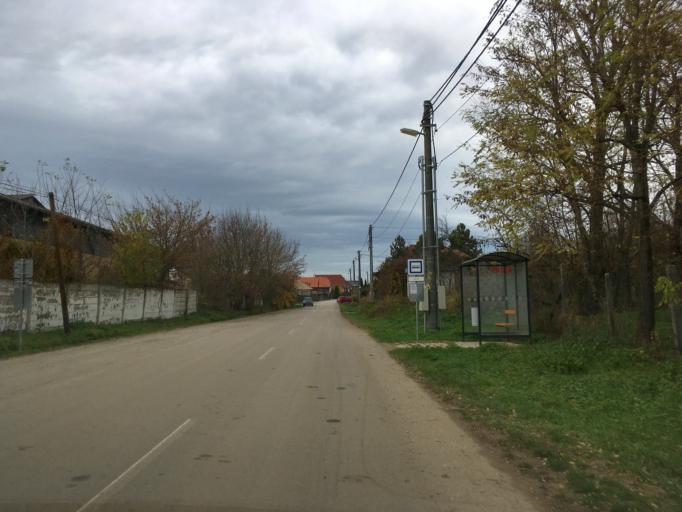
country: SK
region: Nitriansky
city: Svodin
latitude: 48.0185
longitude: 18.4094
